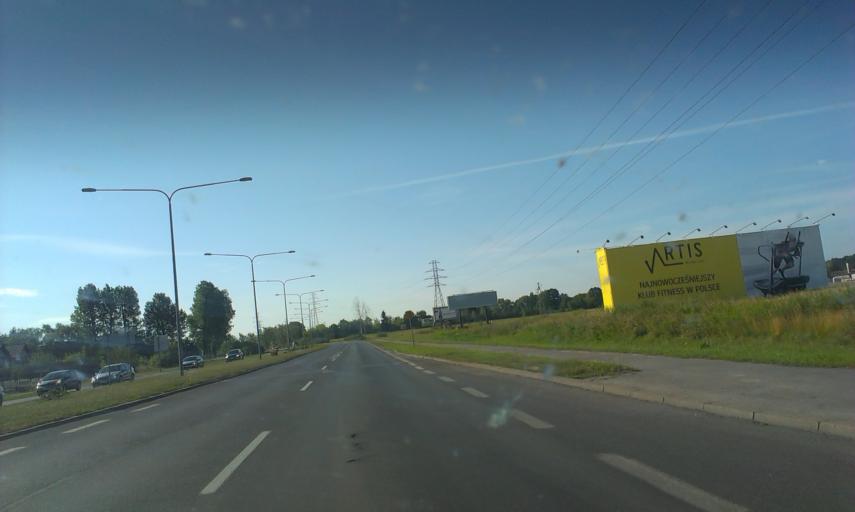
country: PL
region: Masovian Voivodeship
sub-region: Warszawa
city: Kabaty
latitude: 52.1219
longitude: 21.0982
